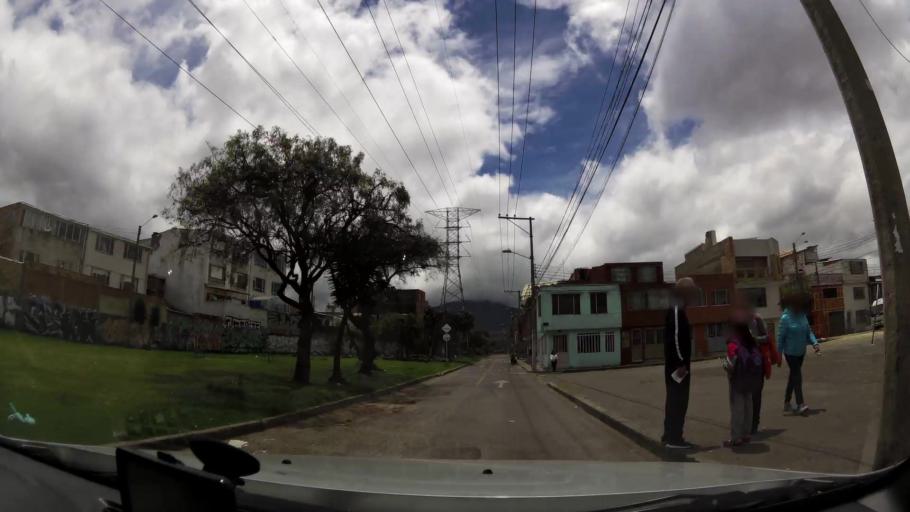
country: CO
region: Bogota D.C.
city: Bogota
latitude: 4.6099
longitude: -74.1108
